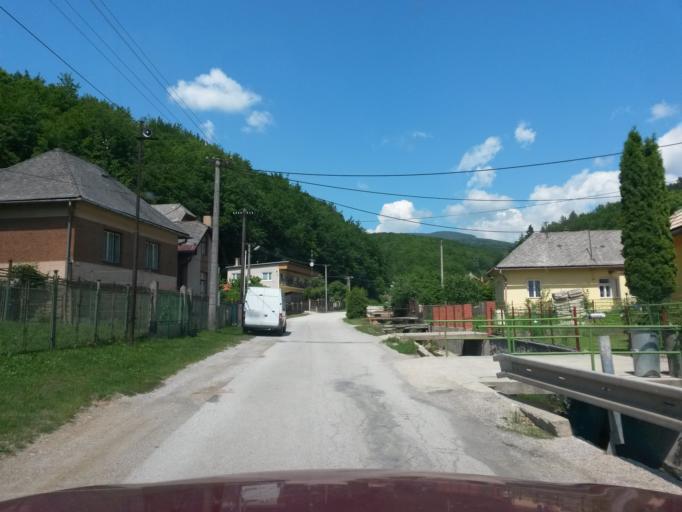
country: SK
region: Kosicky
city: Roznava
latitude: 48.6954
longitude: 20.5455
